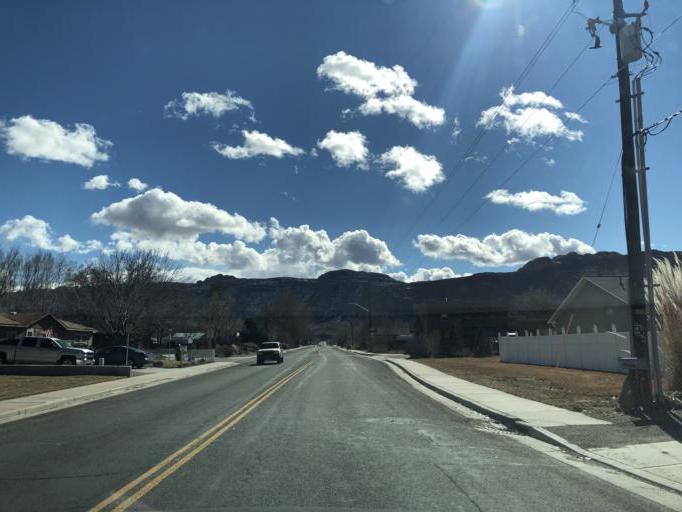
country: US
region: Utah
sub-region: Grand County
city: Moab
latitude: 38.5832
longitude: -109.5611
